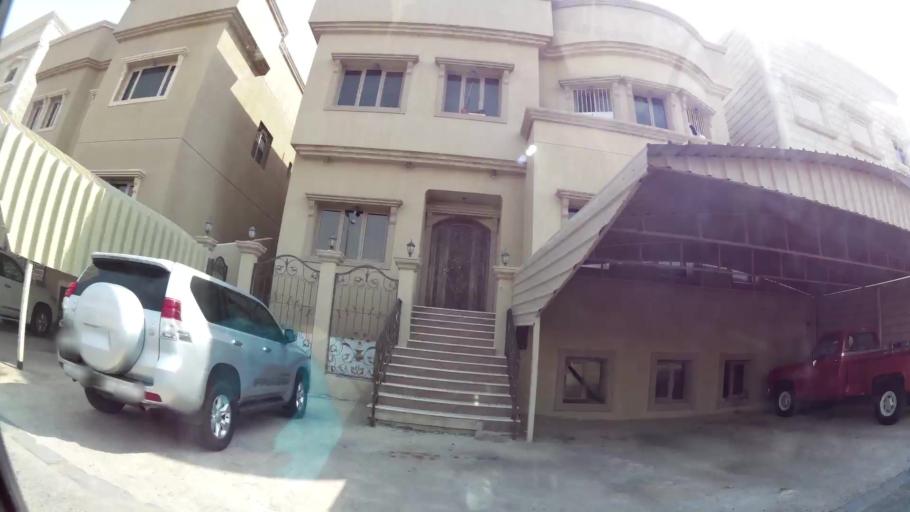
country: KW
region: Muhafazat al Jahra'
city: Al Jahra'
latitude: 29.3094
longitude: 47.7020
